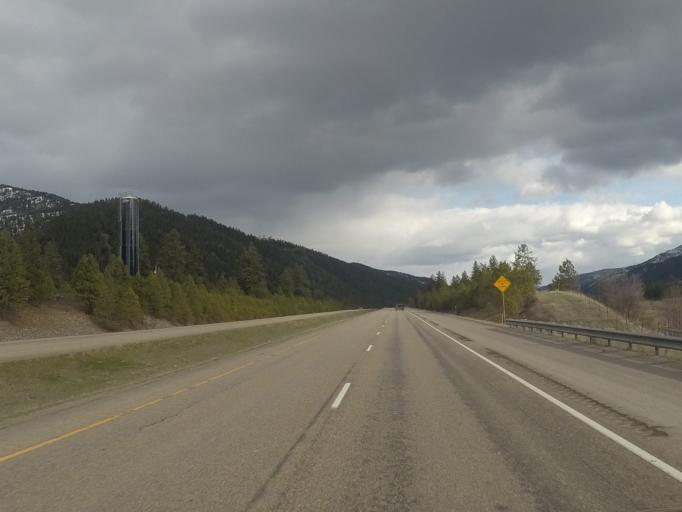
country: US
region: Montana
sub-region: Missoula County
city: Bonner-West Riverside
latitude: 46.8682
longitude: -113.8799
